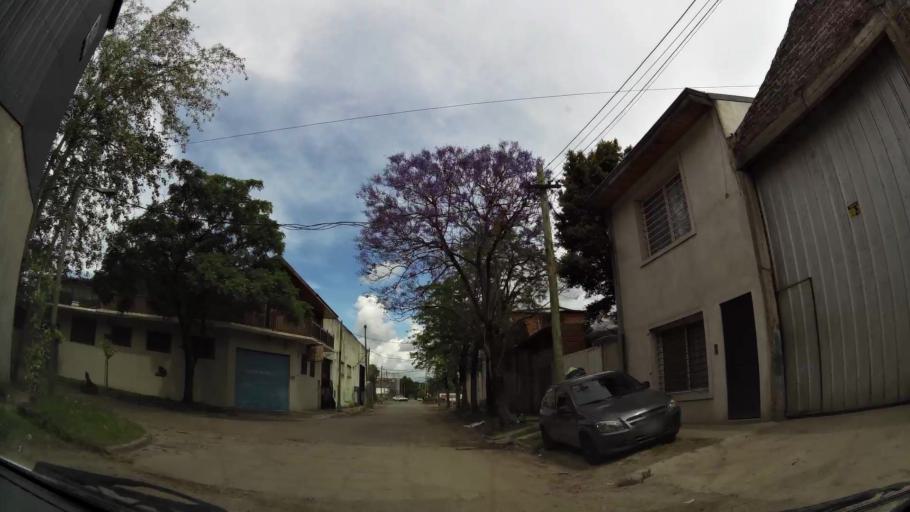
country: AR
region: Buenos Aires
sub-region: Partido de Quilmes
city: Quilmes
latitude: -34.7728
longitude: -58.2766
